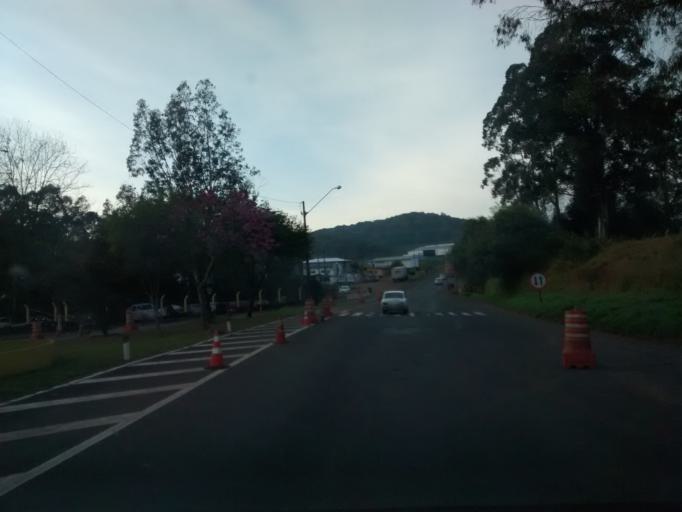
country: BR
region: Parana
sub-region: Francisco Beltrao
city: Francisco Beltrao
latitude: -26.1150
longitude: -53.0419
